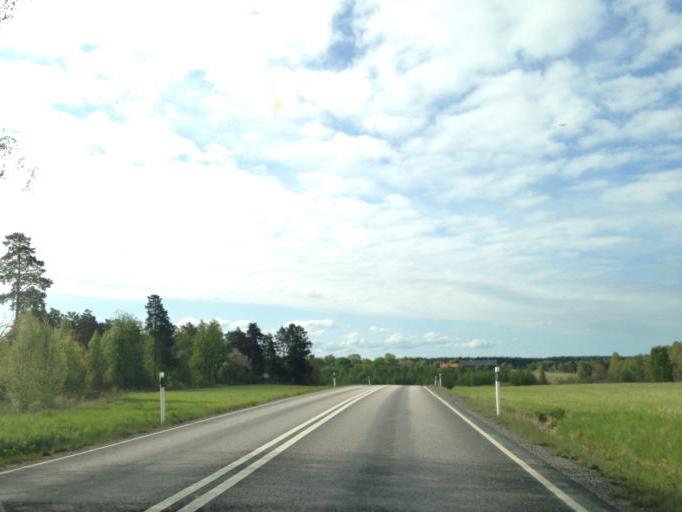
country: SE
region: Soedermanland
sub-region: Flens Kommun
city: Malmkoping
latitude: 58.9882
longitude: 16.8422
